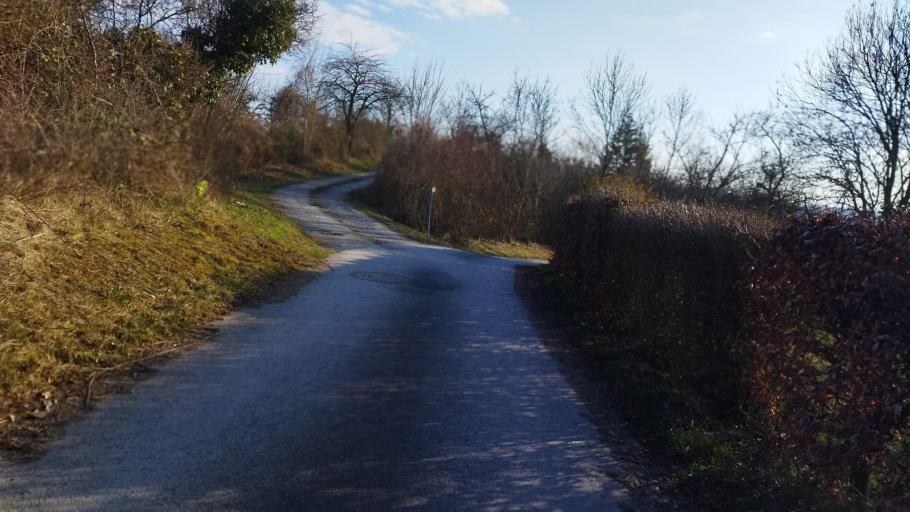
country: DE
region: Baden-Wuerttemberg
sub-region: Regierungsbezirk Stuttgart
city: Walheim
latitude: 49.0130
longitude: 9.1634
